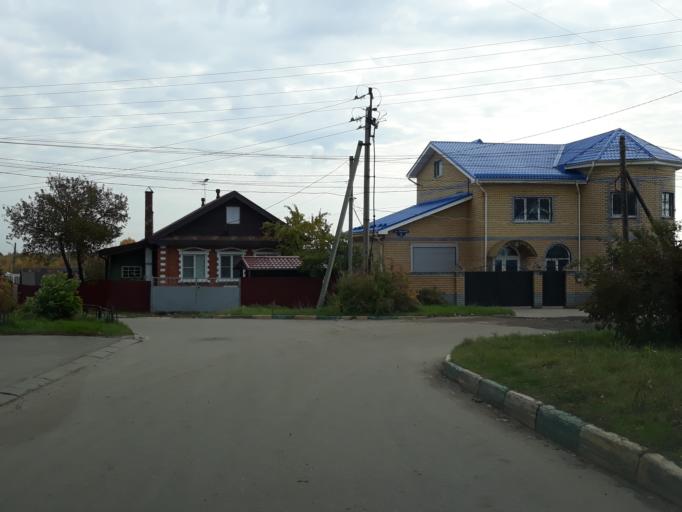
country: RU
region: Nizjnij Novgorod
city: Nizhniy Novgorod
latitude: 56.2375
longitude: 43.9793
